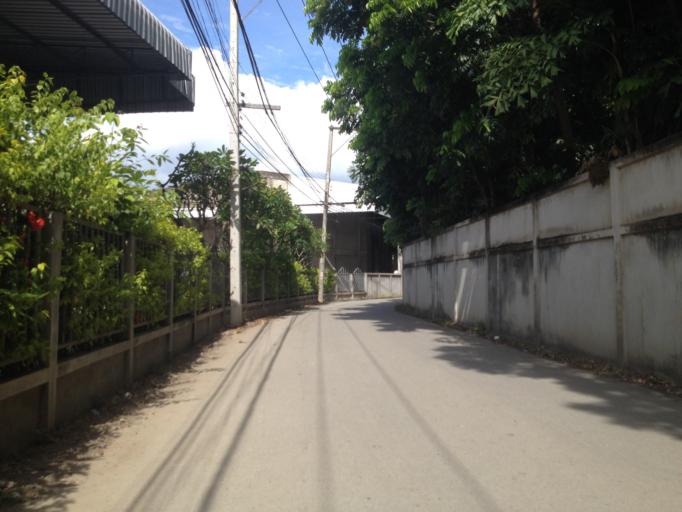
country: TH
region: Chiang Mai
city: Hang Dong
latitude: 18.7153
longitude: 98.9347
